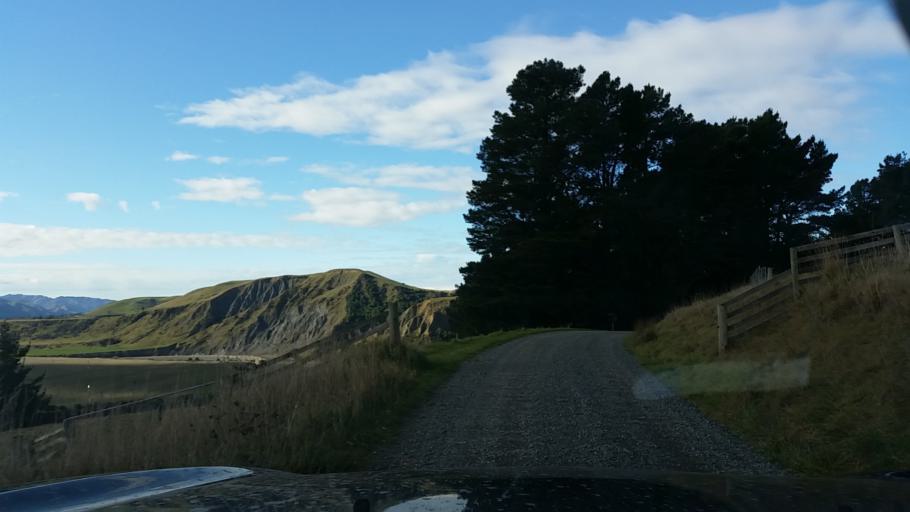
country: NZ
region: Marlborough
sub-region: Marlborough District
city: Blenheim
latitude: -41.7659
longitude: 173.8580
